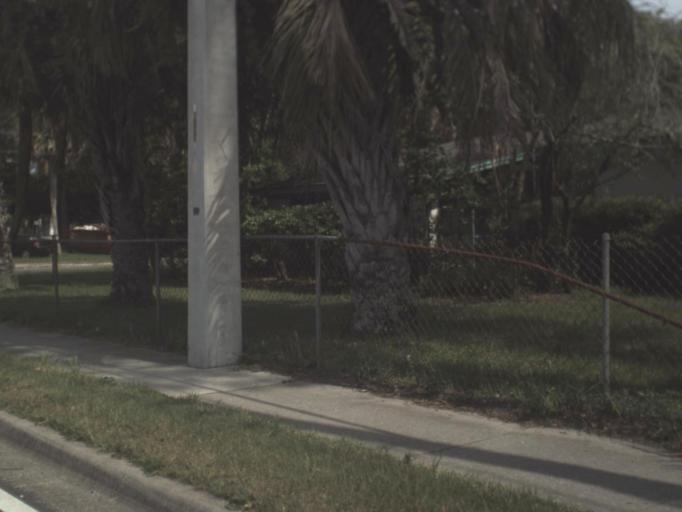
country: US
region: Florida
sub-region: Clay County
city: Bellair-Meadowbrook Terrace
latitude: 30.2483
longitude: -81.7503
